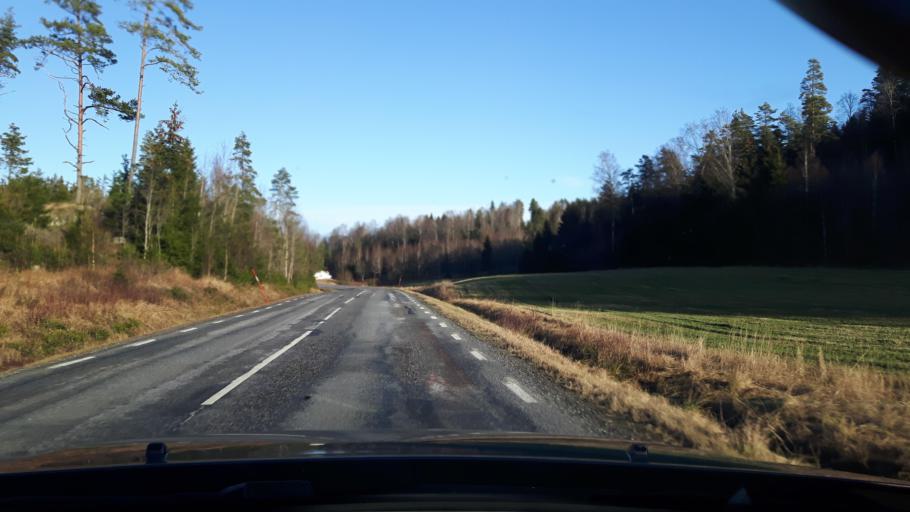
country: SE
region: Vaestra Goetaland
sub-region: Munkedals Kommun
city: Munkedal
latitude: 58.5870
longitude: 11.7426
